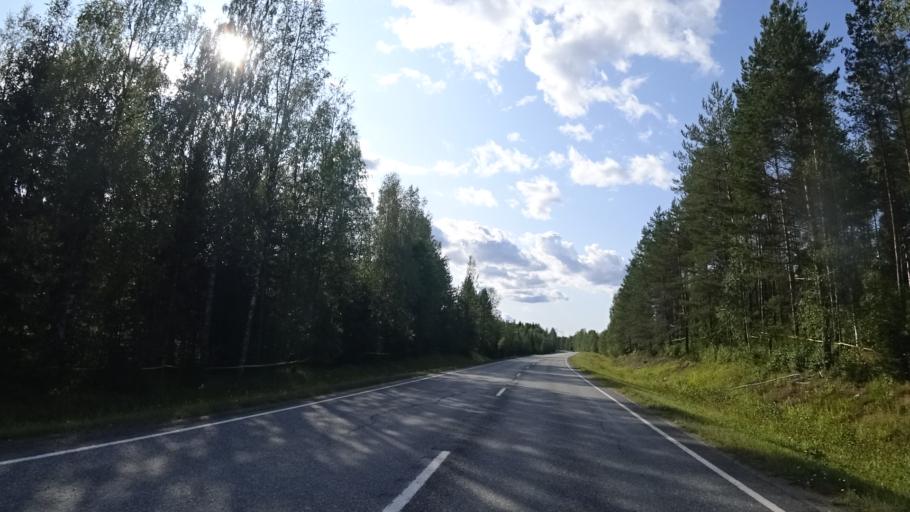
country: FI
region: North Karelia
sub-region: Keski-Karjala
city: Kitee
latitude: 62.0951
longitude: 30.0895
